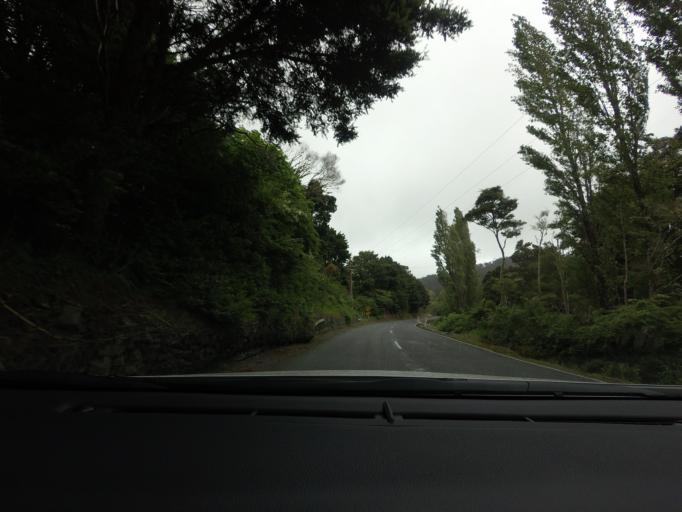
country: NZ
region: Auckland
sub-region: Auckland
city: Wellsford
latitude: -36.2816
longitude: 174.5990
